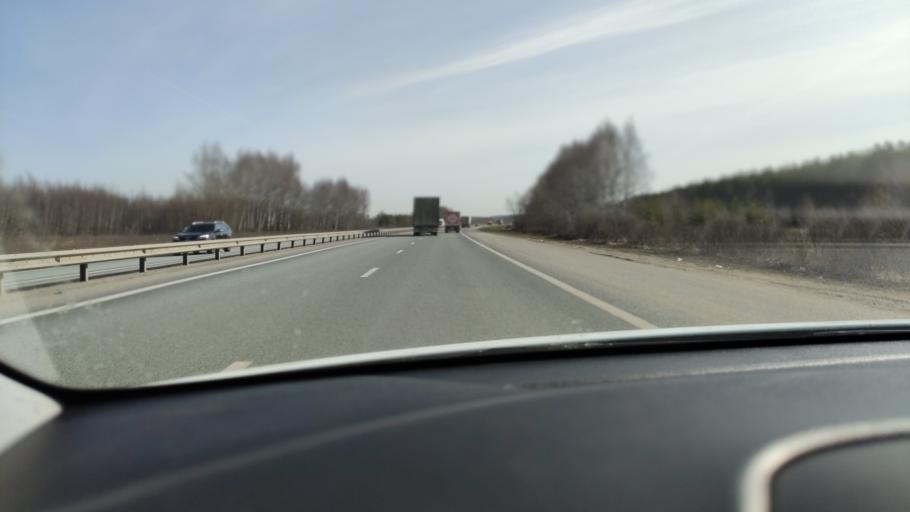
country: RU
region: Tatarstan
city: Staroye Arakchino
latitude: 55.9047
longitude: 48.9797
